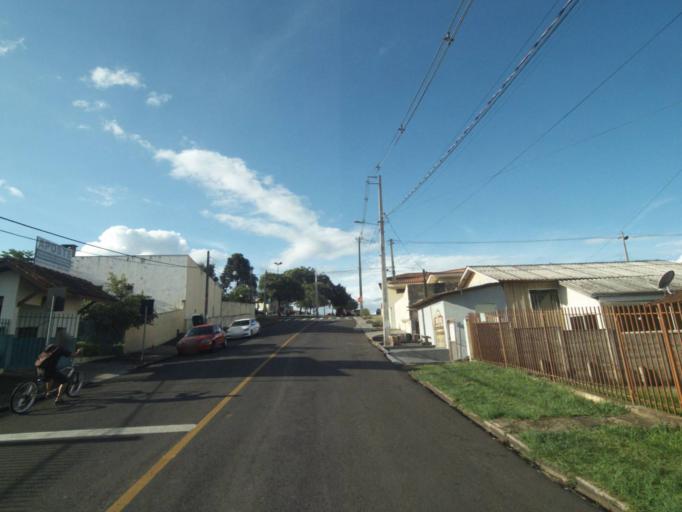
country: BR
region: Parana
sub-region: Telemaco Borba
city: Telemaco Borba
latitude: -24.3373
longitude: -50.6210
